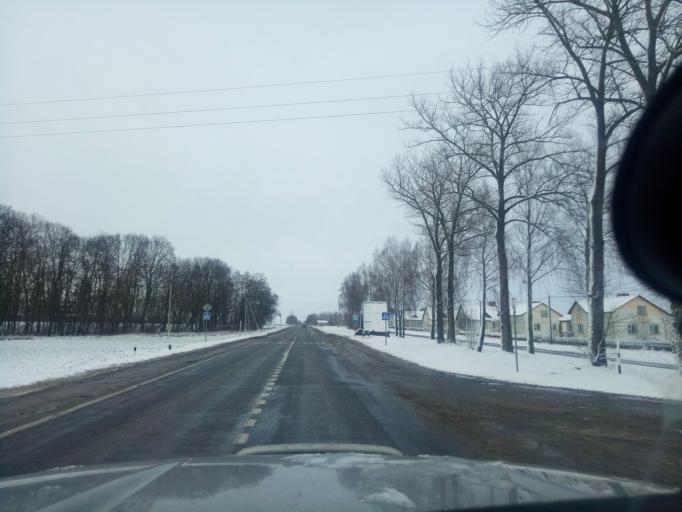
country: BY
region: Minsk
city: Tsimkavichy
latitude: 53.0819
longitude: 27.0105
